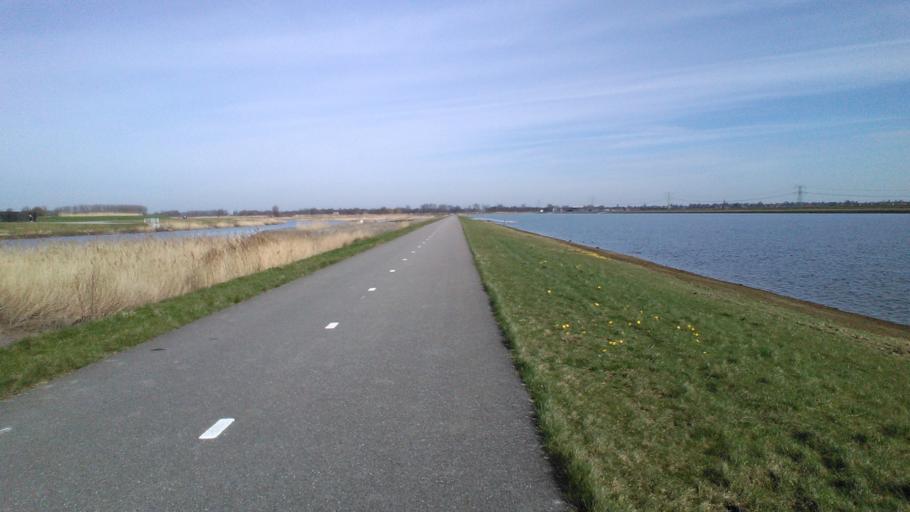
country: NL
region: South Holland
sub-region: Gemeente Lansingerland
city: Bleiswijk
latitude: 51.9957
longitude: 4.5586
